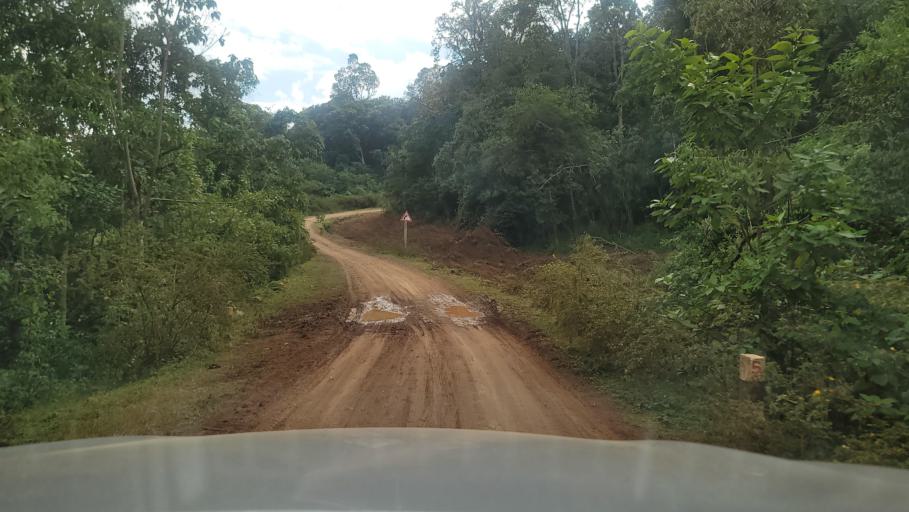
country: ET
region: Southern Nations, Nationalities, and People's Region
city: Bonga
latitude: 7.6706
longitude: 36.2438
